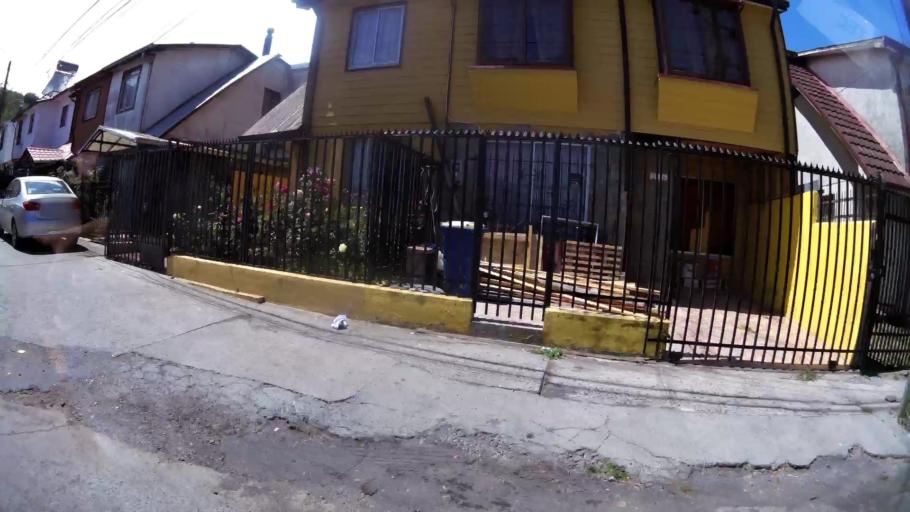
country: CL
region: Biobio
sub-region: Provincia de Concepcion
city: Concepcion
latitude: -36.8018
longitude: -73.0462
